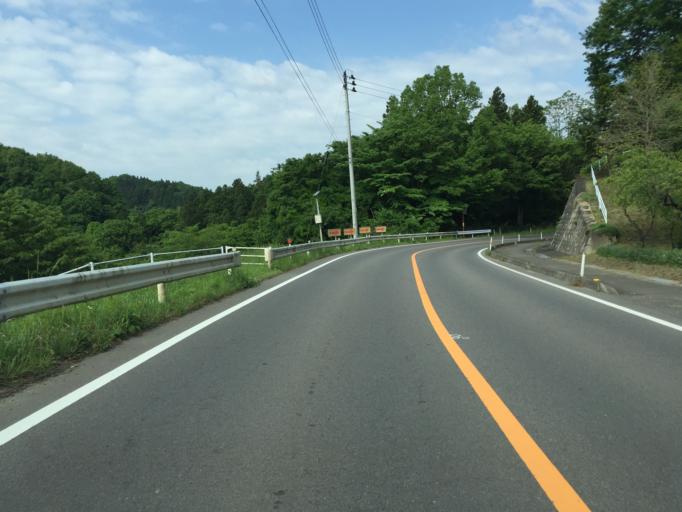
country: JP
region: Fukushima
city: Fukushima-shi
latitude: 37.6599
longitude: 140.5104
